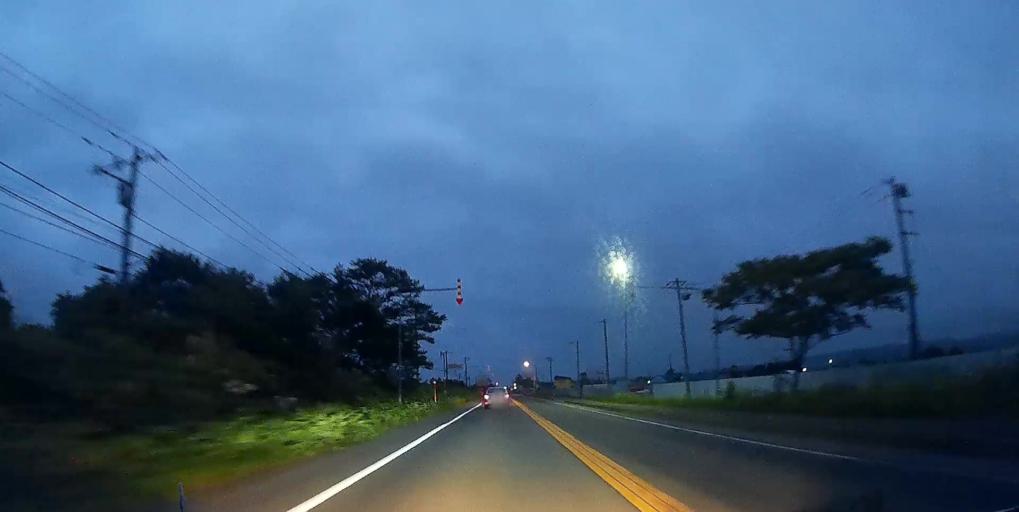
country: JP
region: Hokkaido
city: Nanae
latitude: 42.2210
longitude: 140.3734
